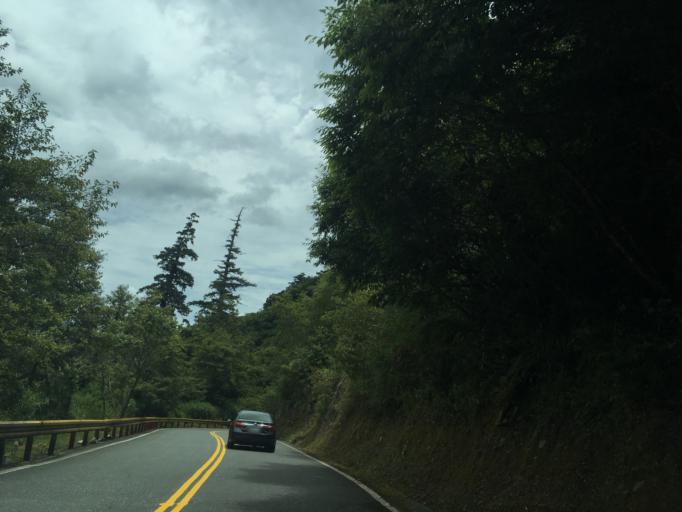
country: TW
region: Taiwan
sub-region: Hualien
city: Hualian
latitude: 24.1777
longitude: 121.3888
